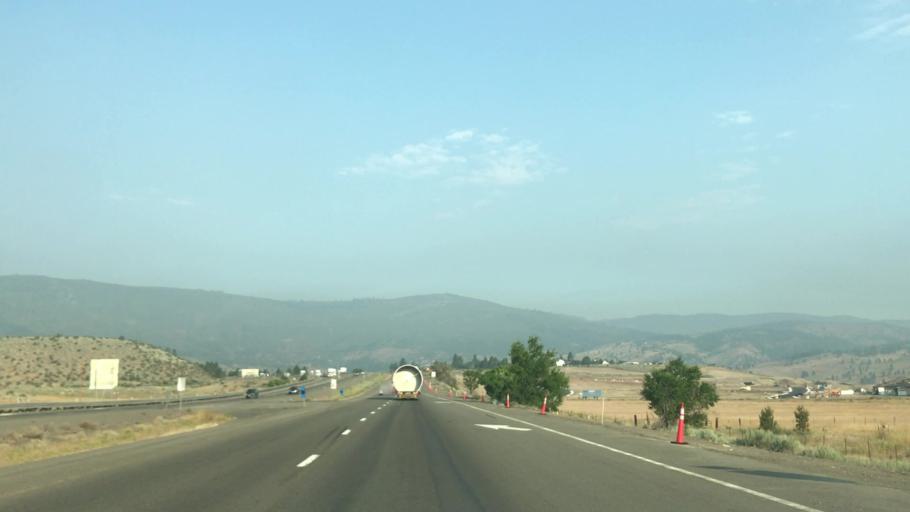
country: US
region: Nevada
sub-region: Washoe County
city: Verdi
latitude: 39.5128
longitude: -119.9721
